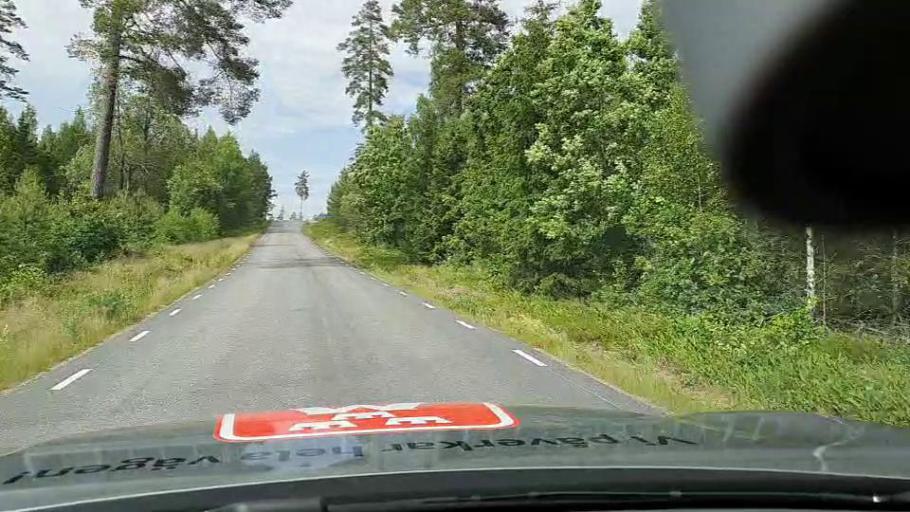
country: SE
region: Soedermanland
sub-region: Eskilstuna Kommun
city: Arla
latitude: 59.2401
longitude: 16.7216
